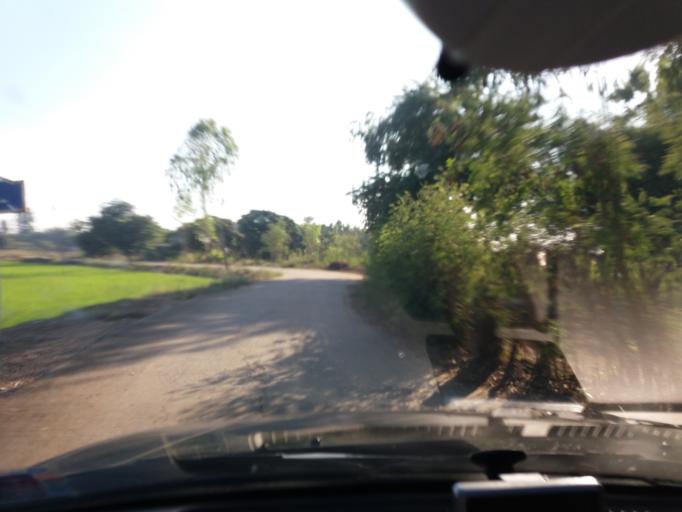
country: TH
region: Suphan Buri
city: Doem Bang Nang Buat
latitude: 14.9119
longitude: 100.1307
